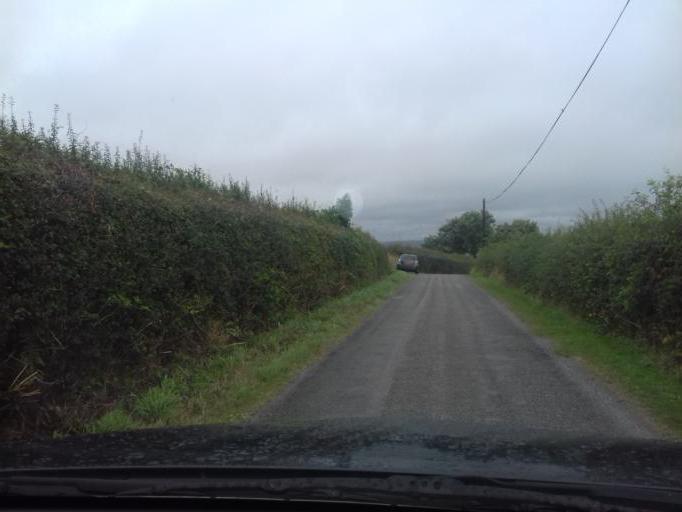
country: IE
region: Leinster
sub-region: Kilkenny
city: Graiguenamanagh
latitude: 52.5968
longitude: -7.0110
